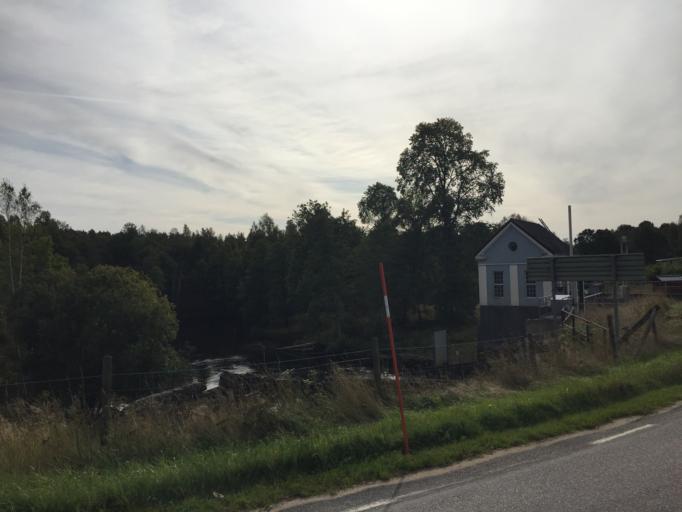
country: SE
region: Joenkoeping
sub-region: Varnamo Kommun
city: Varnamo
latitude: 57.2634
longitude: 14.0569
